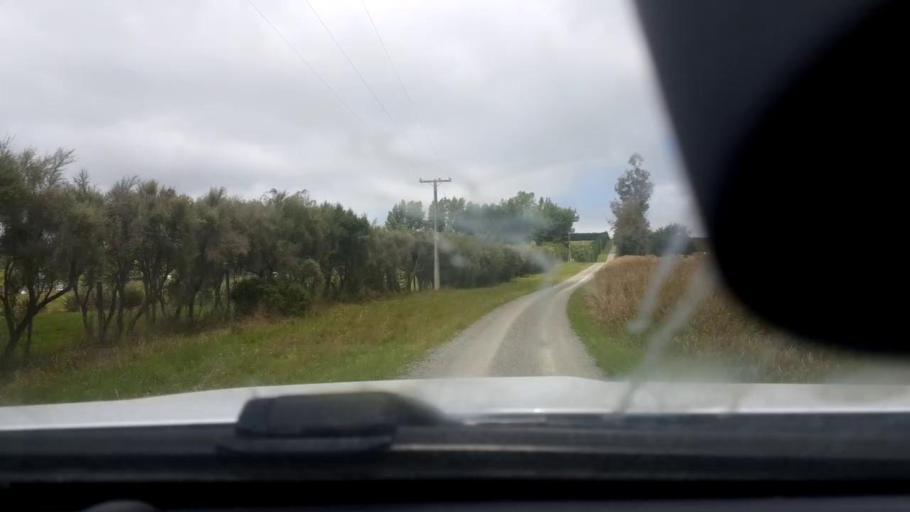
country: NZ
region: Canterbury
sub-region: Timaru District
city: Pleasant Point
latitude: -44.1648
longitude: 171.1474
